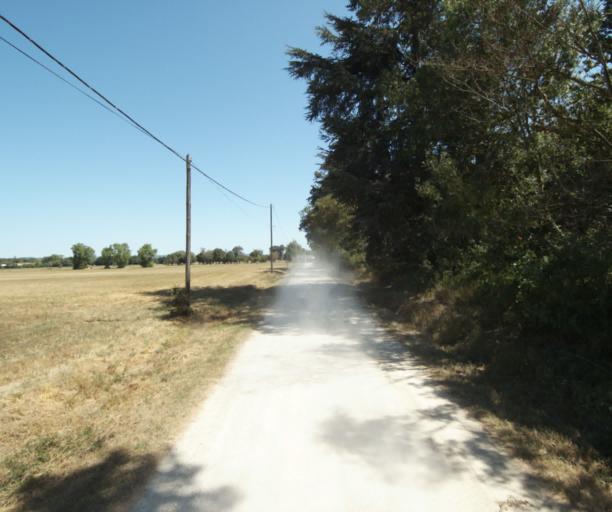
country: FR
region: Midi-Pyrenees
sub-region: Departement de la Haute-Garonne
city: Revel
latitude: 43.4818
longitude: 1.9669
